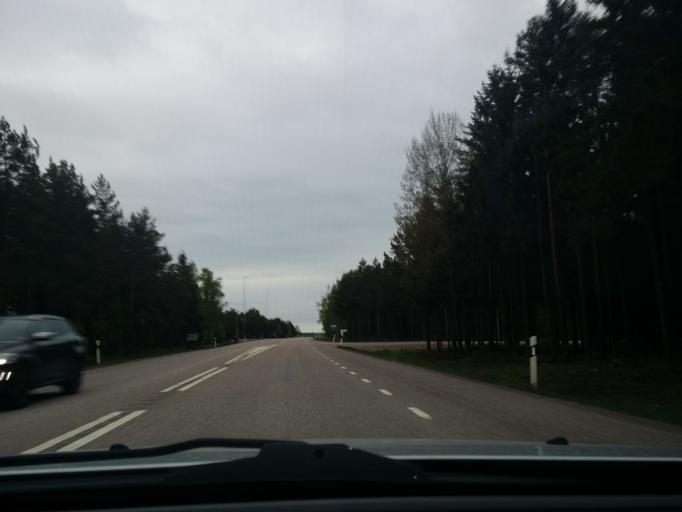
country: SE
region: Vaestmanland
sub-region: Hallstahammars Kommun
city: Kolback
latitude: 59.5681
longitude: 16.3498
